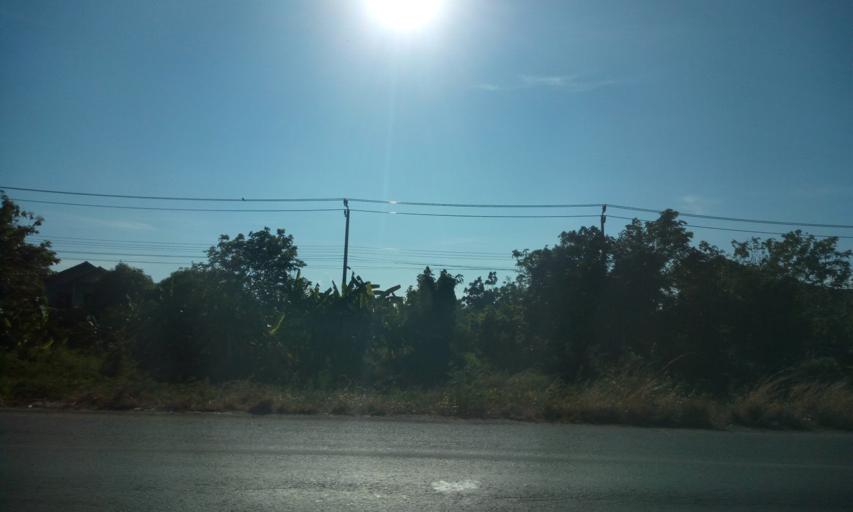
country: TH
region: Samut Prakan
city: Bang Bo District
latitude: 13.5705
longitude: 100.7563
